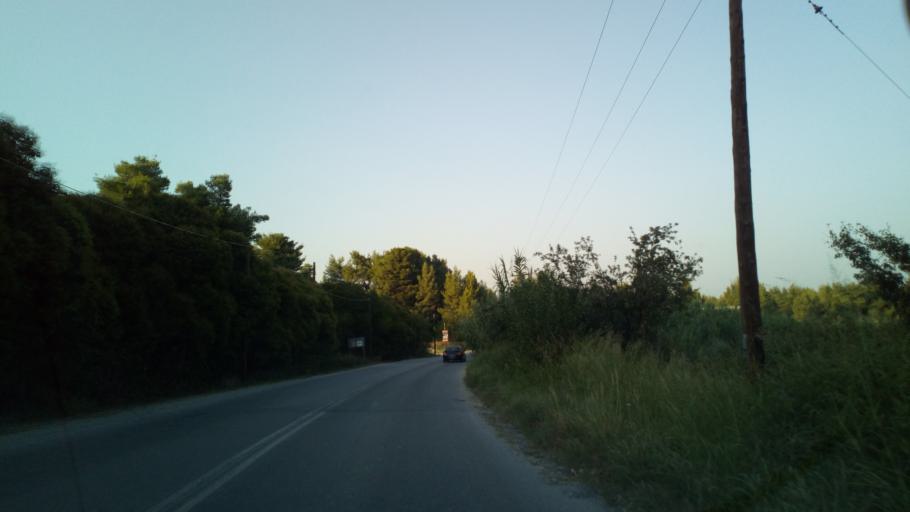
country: GR
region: Central Macedonia
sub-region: Nomos Chalkidikis
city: Pefkochori
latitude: 39.9525
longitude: 23.6710
